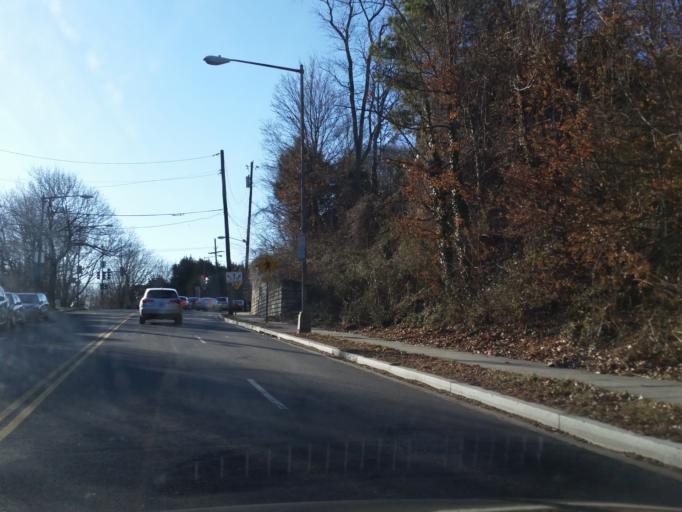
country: US
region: Virginia
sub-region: Arlington County
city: Arlington
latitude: 38.9126
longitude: -77.0837
